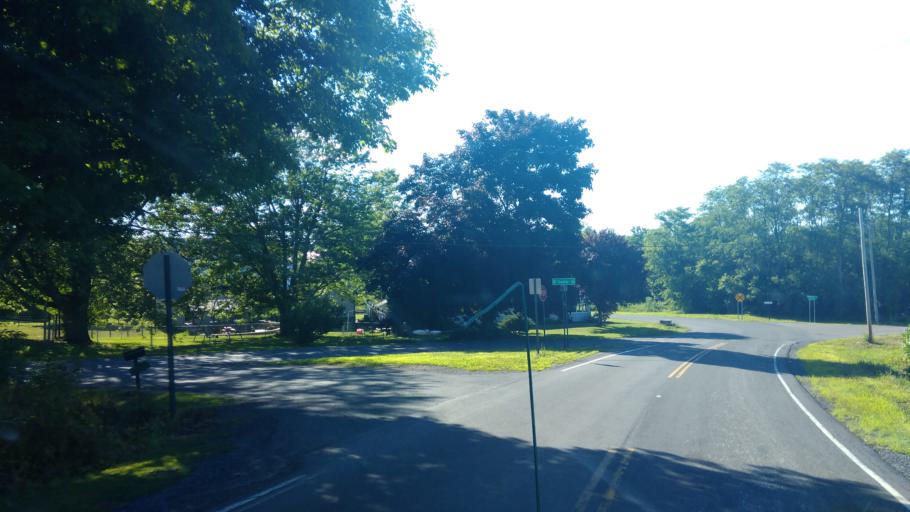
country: US
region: New York
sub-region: Wayne County
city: Lyons
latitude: 43.0031
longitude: -76.9635
